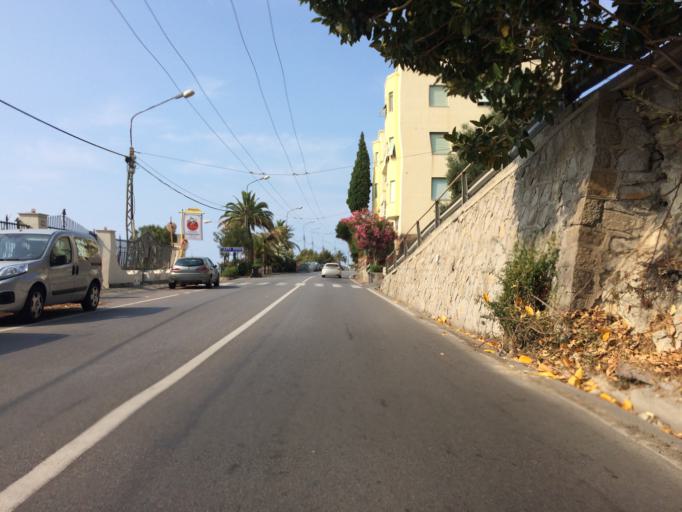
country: IT
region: Liguria
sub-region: Provincia di Imperia
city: Ospedaletti
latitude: 43.7989
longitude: 7.7409
